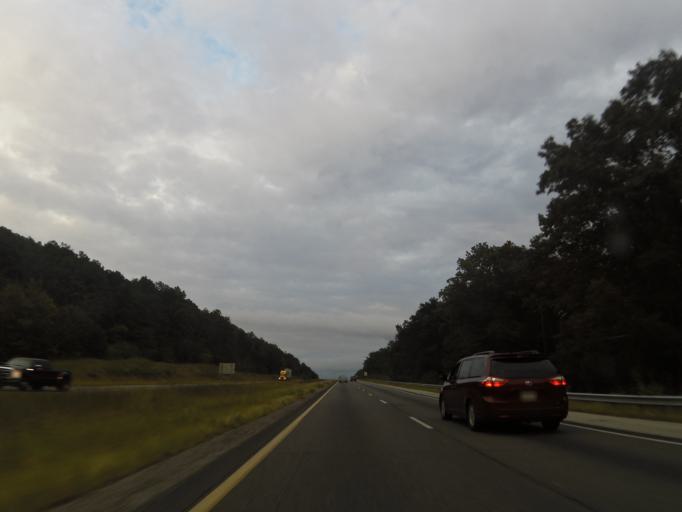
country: US
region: Alabama
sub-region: Saint Clair County
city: Springville
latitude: 33.7713
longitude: -86.4576
